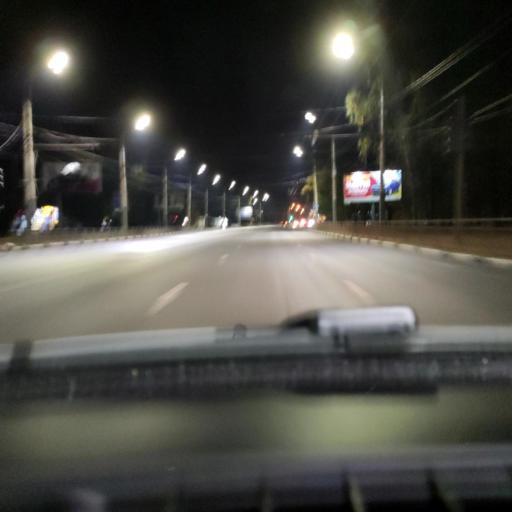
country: RU
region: Voronezj
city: Voronezh
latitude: 51.6654
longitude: 39.2449
